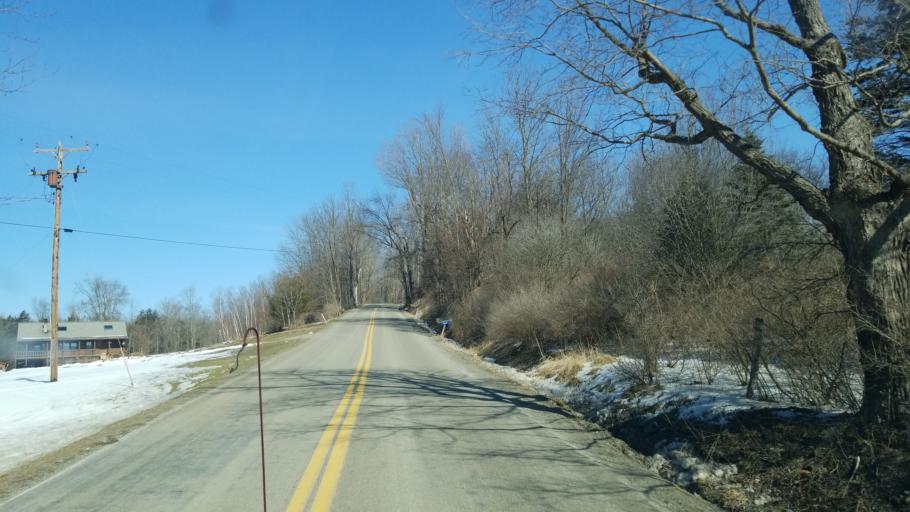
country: US
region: Pennsylvania
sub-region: Tioga County
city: Westfield
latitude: 41.9982
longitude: -77.4893
